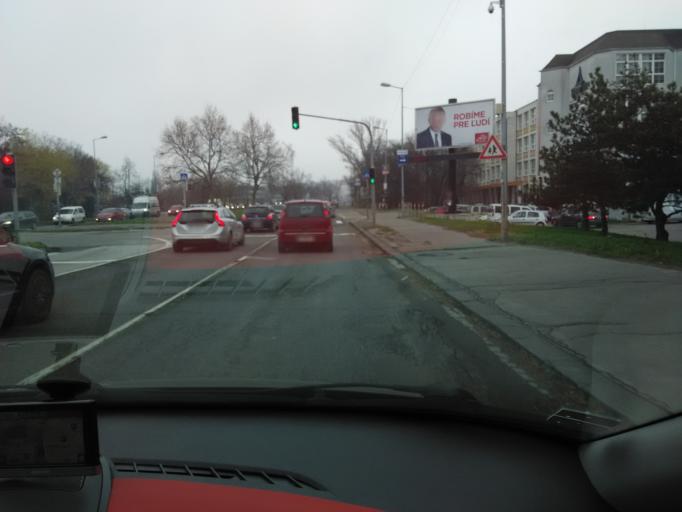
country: SK
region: Bratislavsky
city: Bratislava
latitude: 48.1585
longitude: 17.1432
